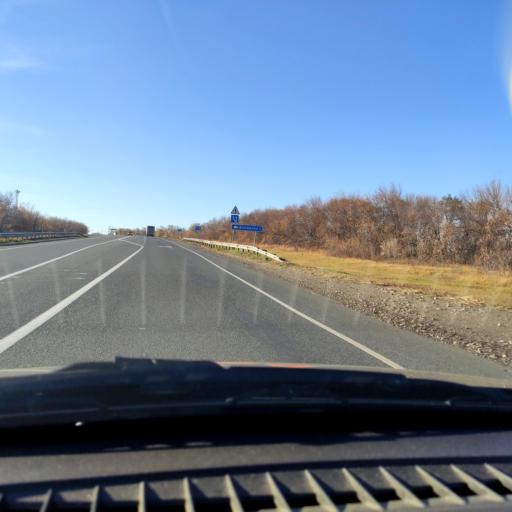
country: RU
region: Samara
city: Mezhdurechensk
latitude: 53.2544
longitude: 49.1422
